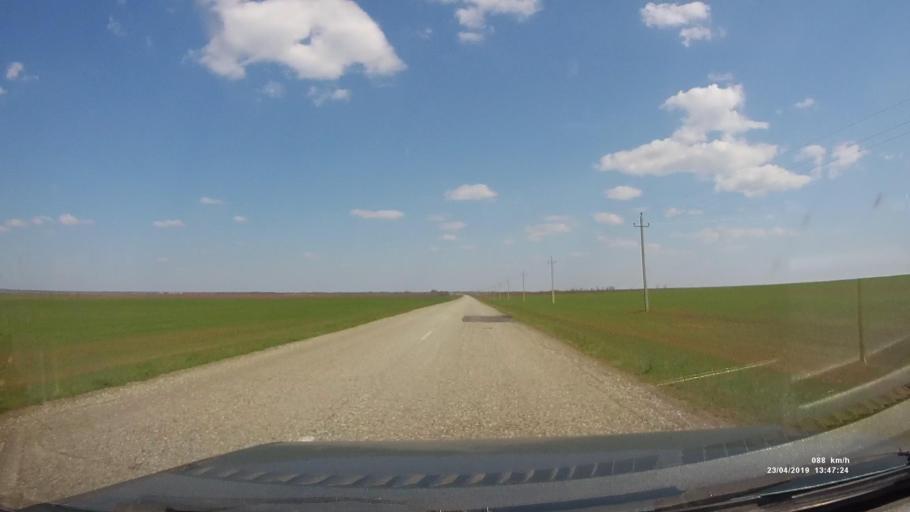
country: RU
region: Kalmykiya
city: Yashalta
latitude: 46.5995
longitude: 42.8530
